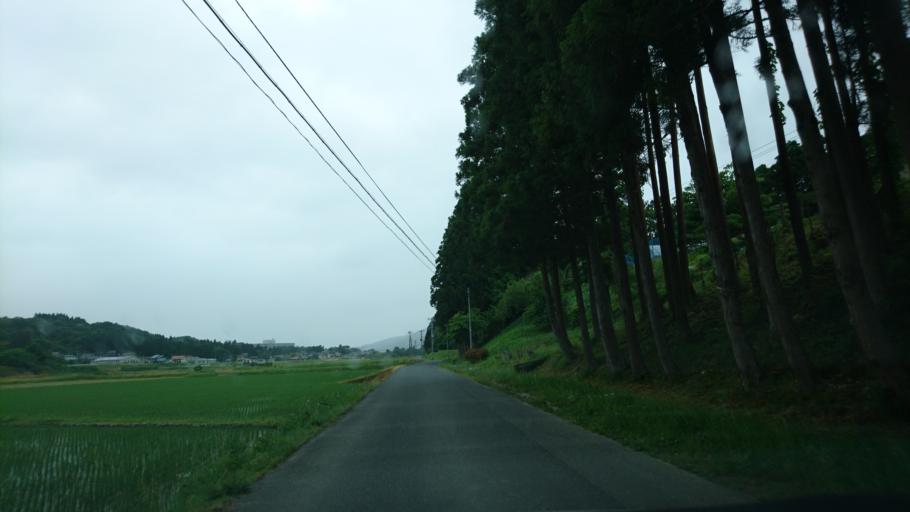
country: JP
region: Iwate
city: Ichinoseki
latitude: 38.9242
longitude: 141.1764
